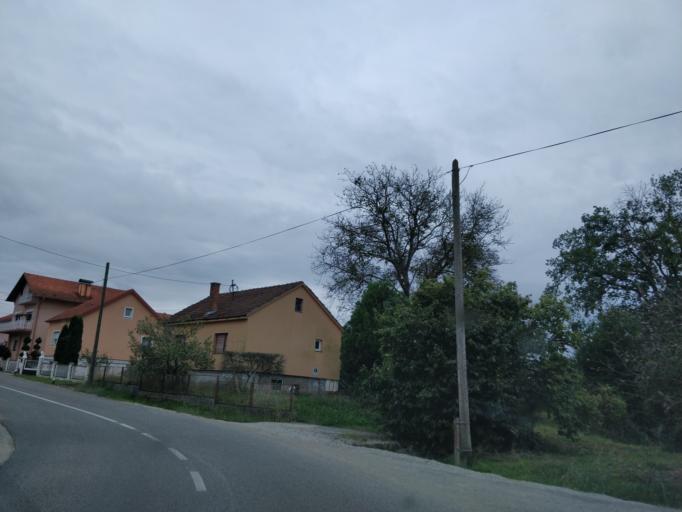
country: HR
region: Zagrebacka
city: Jakovlje
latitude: 45.9506
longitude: 15.8457
